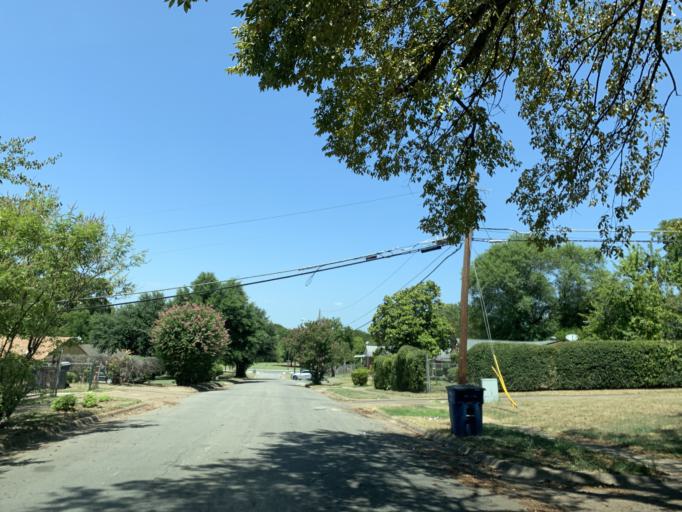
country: US
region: Texas
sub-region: Dallas County
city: Hutchins
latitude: 32.6803
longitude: -96.7654
